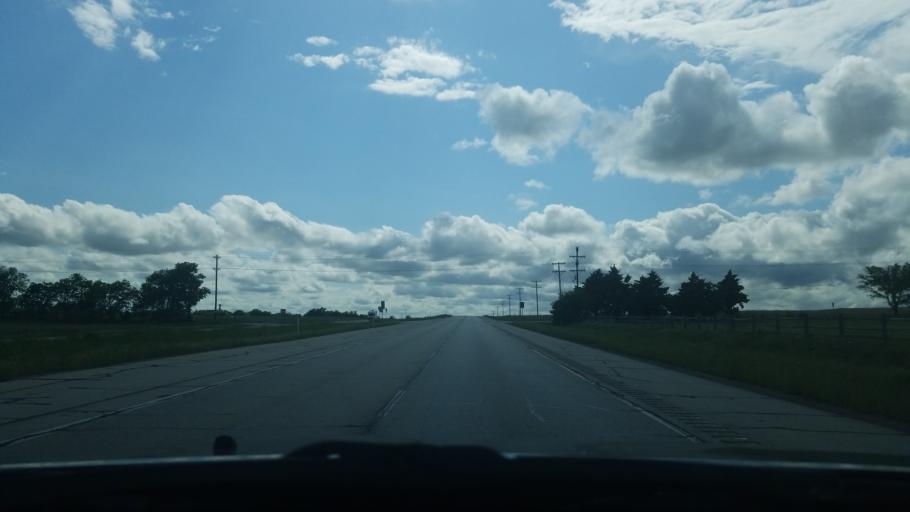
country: US
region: Texas
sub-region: Wise County
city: New Fairview
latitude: 33.2497
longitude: -97.4266
